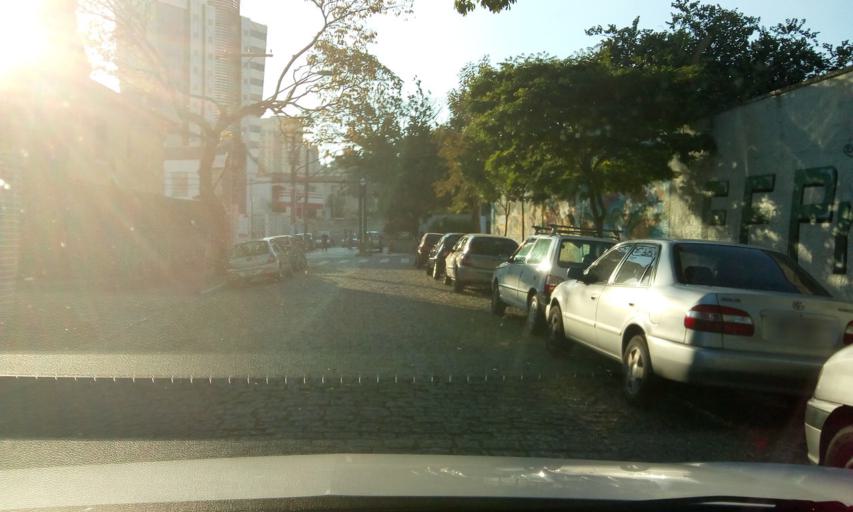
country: BR
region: Sao Paulo
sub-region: Sao Paulo
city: Sao Paulo
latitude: -23.4932
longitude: -46.6164
